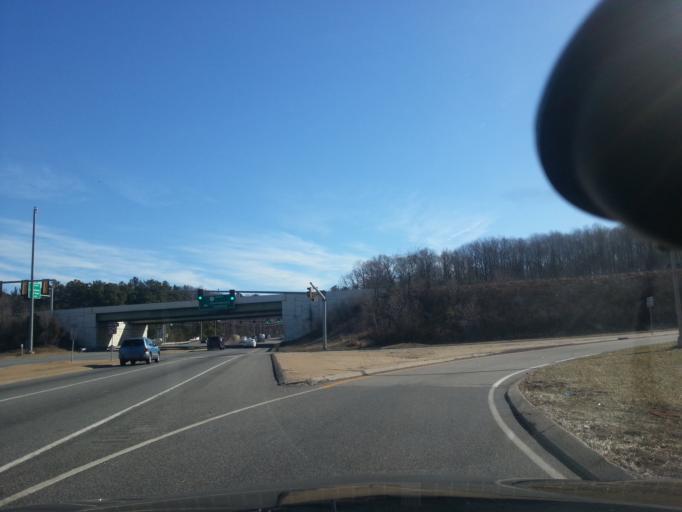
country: US
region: Delaware
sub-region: New Castle County
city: Bear
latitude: 39.6605
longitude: -75.6537
